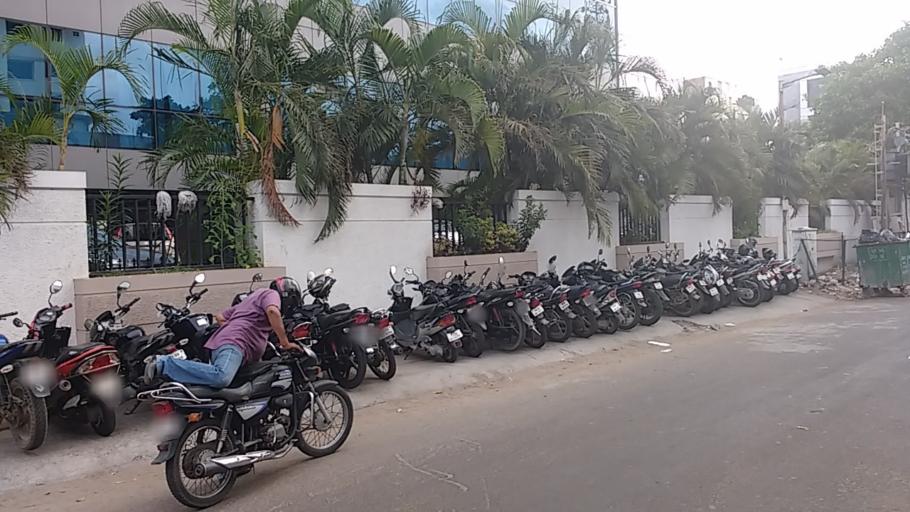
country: IN
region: Tamil Nadu
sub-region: Chennai
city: Chetput
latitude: 13.0472
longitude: 80.2194
